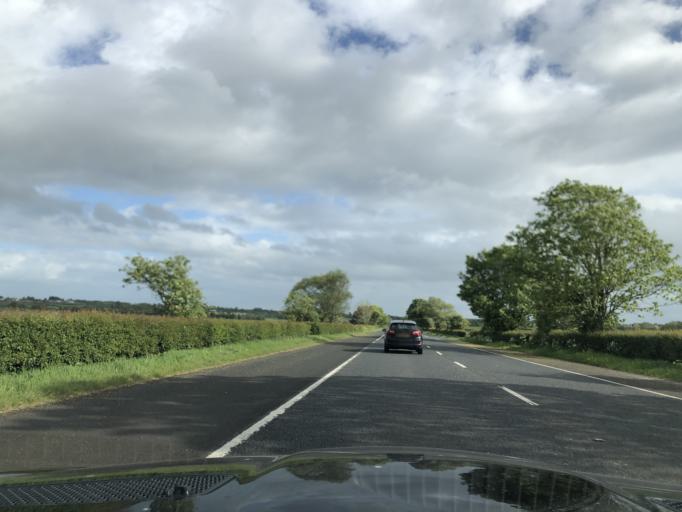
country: GB
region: Northern Ireland
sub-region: Ballymoney District
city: Ballymoney
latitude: 55.0960
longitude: -6.5348
